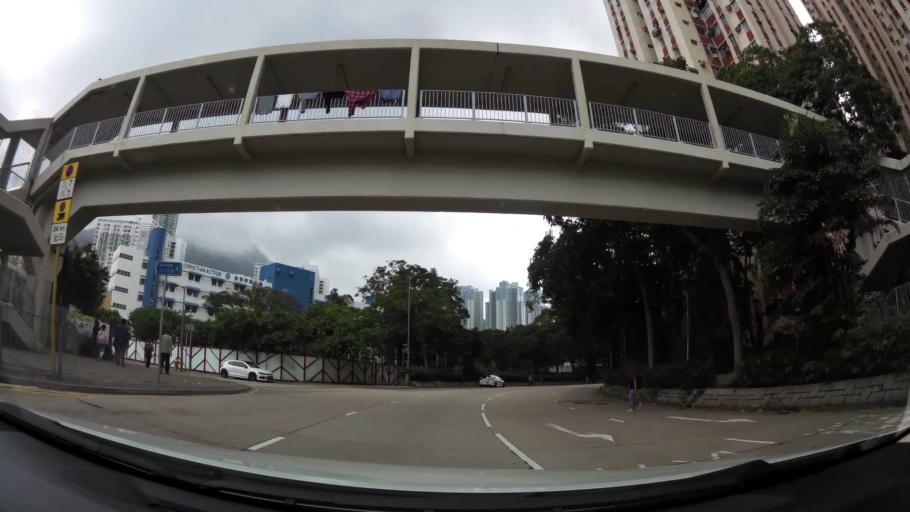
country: HK
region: Kowloon City
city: Kowloon
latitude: 22.3313
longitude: 114.2059
